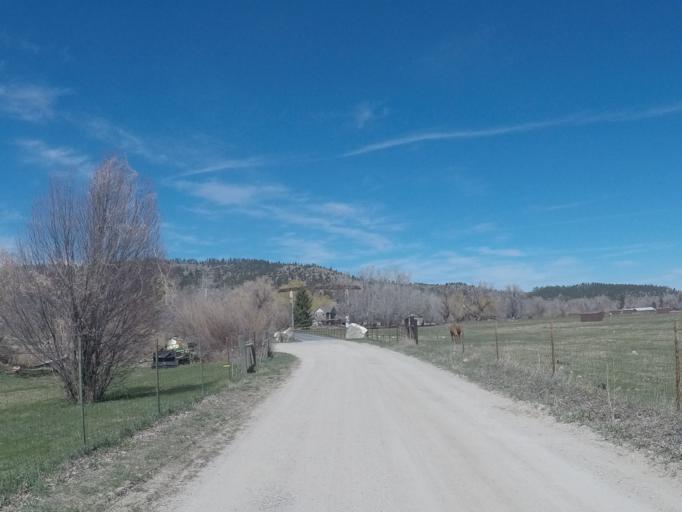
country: US
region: Montana
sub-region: Stillwater County
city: Columbus
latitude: 45.5808
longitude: -109.3291
